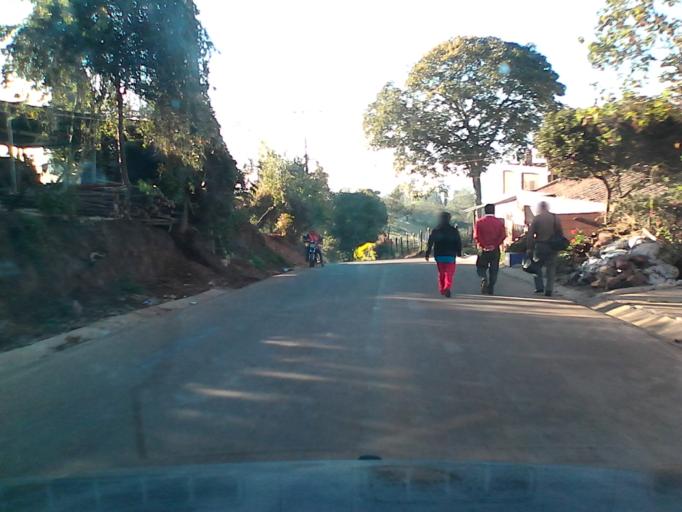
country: CO
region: Boyaca
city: Duitama
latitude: 5.8533
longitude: -73.0353
